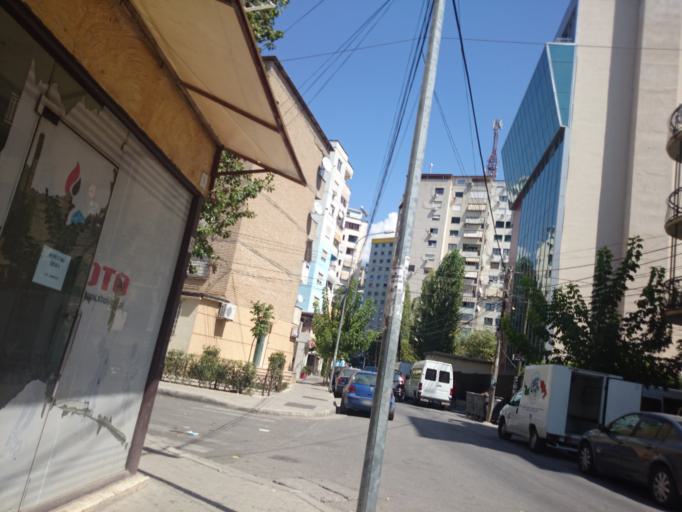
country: AL
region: Tirane
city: Tirana
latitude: 41.3349
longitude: 19.8146
